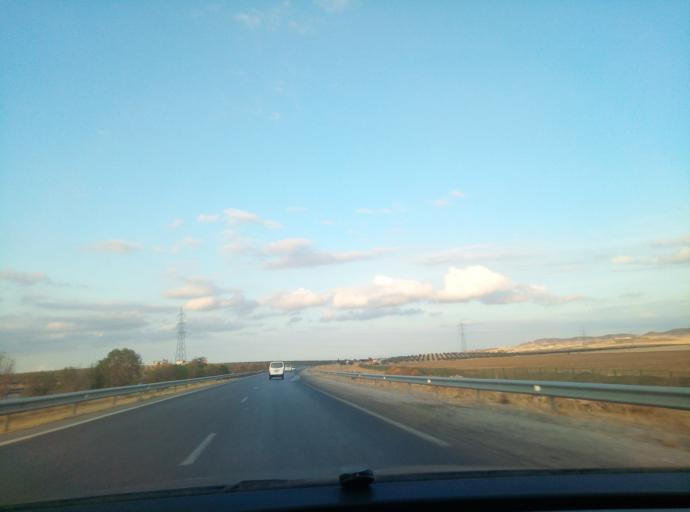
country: TN
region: Manouba
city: El Battan
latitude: 36.6651
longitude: 9.8587
